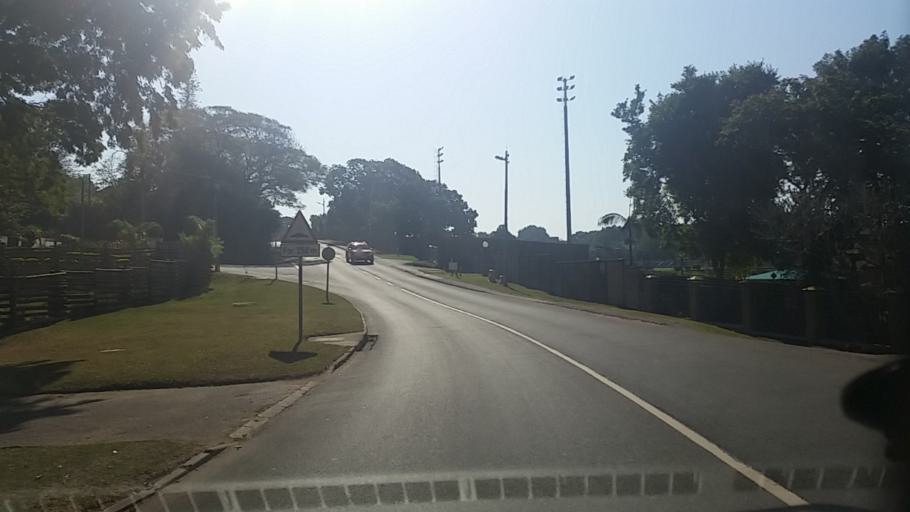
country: ZA
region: KwaZulu-Natal
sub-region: eThekwini Metropolitan Municipality
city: Berea
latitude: -29.8399
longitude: 30.9146
